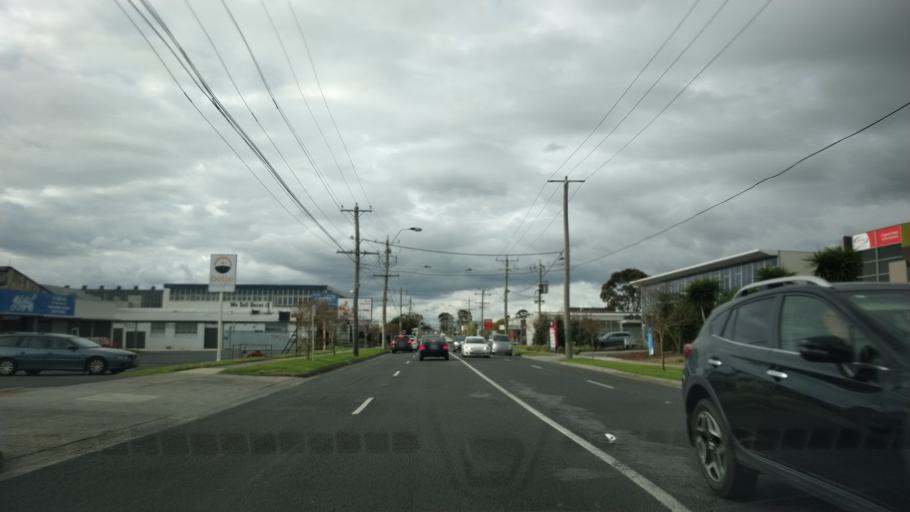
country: AU
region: Victoria
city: Highett
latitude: -37.9497
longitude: 145.0586
